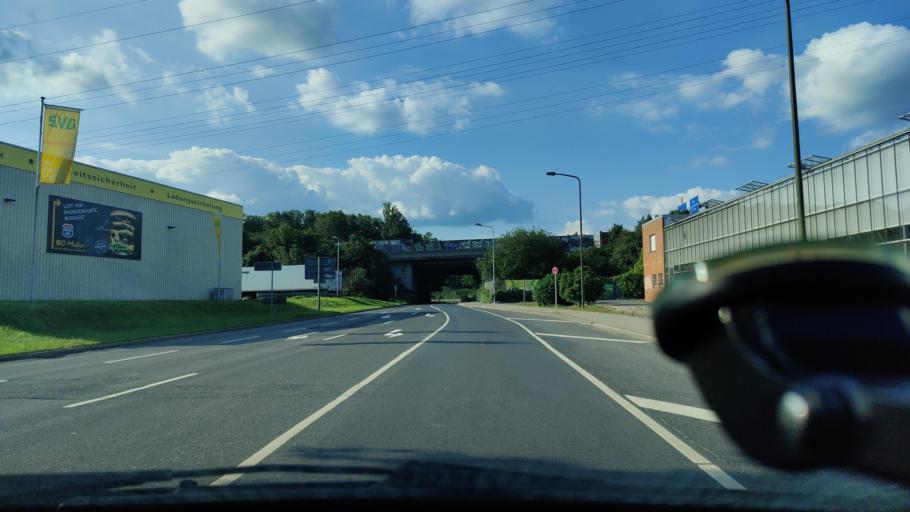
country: DE
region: North Rhine-Westphalia
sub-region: Regierungsbezirk Dusseldorf
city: Erkrath
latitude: 51.1888
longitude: 6.8443
